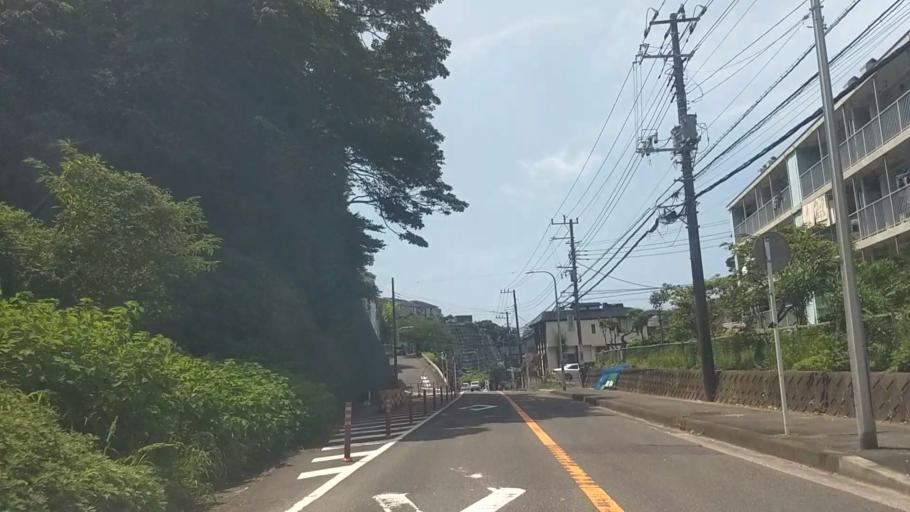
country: JP
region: Kanagawa
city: Kamakura
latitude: 35.3043
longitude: 139.5621
